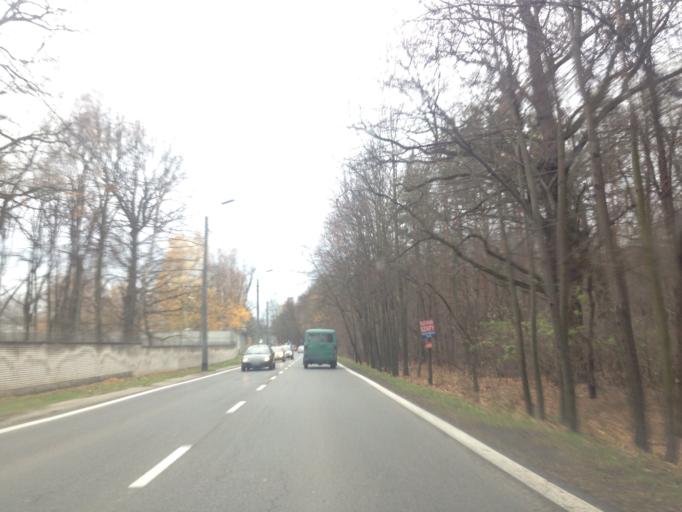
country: PL
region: Masovian Voivodeship
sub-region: Warszawa
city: Rembertow
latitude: 52.2474
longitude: 21.1426
